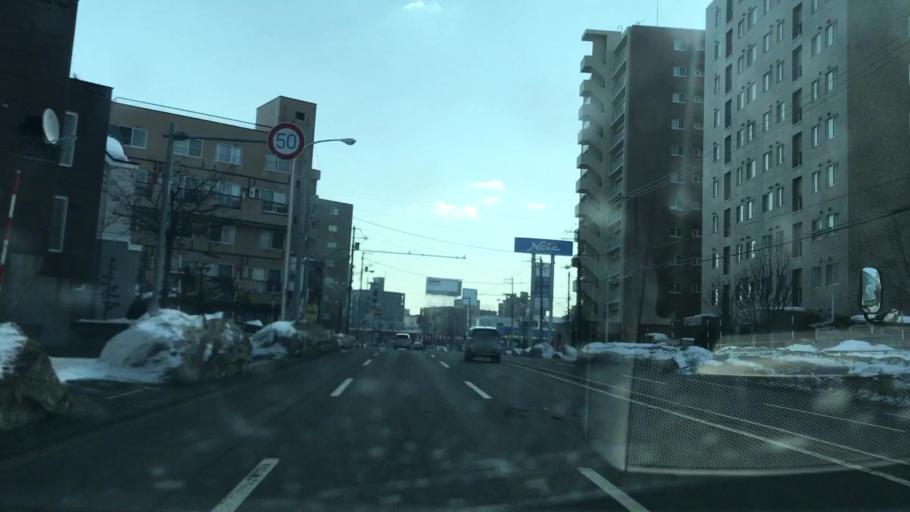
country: JP
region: Hokkaido
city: Sapporo
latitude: 43.0324
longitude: 141.3626
